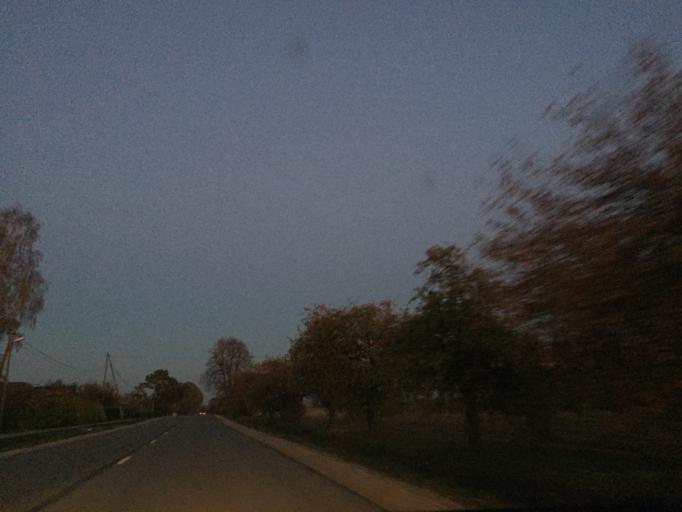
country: LT
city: Zagare
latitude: 56.4842
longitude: 23.1778
